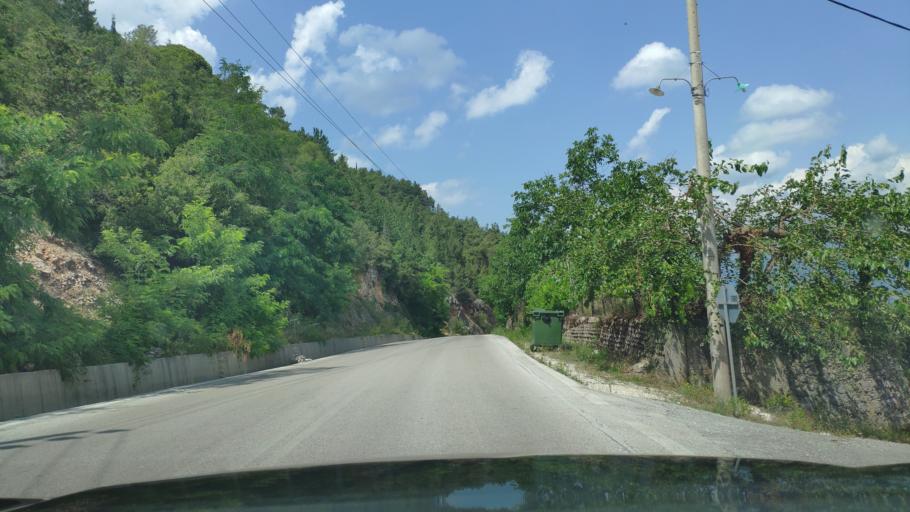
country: GR
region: Epirus
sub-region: Nomos Artas
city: Agios Dimitrios
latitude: 39.3243
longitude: 20.9951
